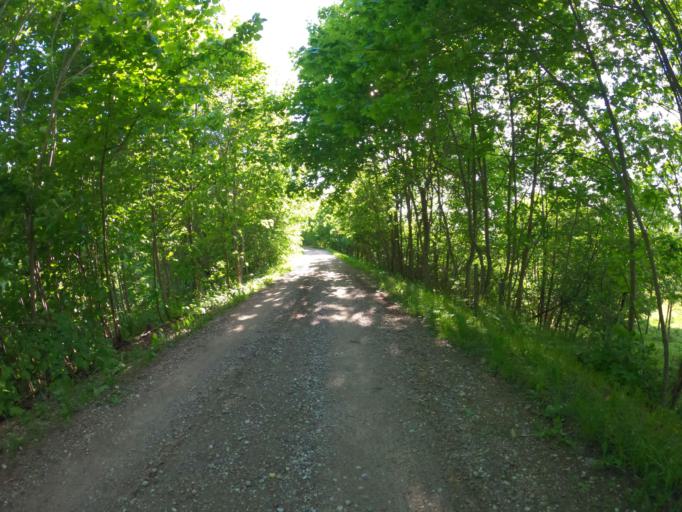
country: PL
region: Warmian-Masurian Voivodeship
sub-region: Powiat lidzbarski
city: Lidzbark Warminski
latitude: 54.1256
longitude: 20.6063
